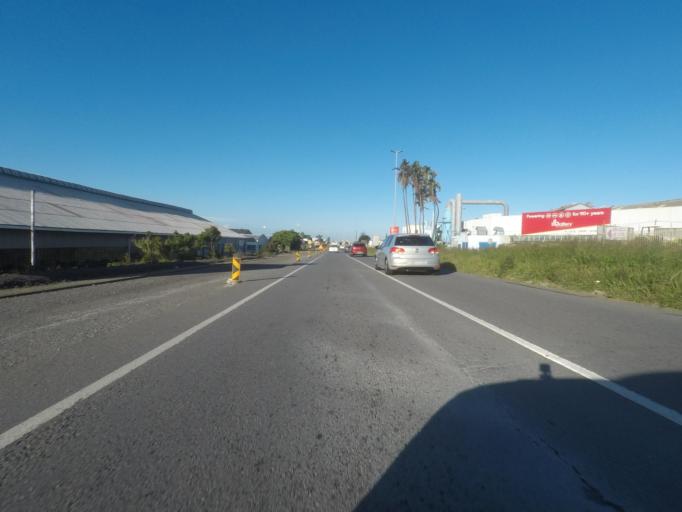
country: ZA
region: Eastern Cape
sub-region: Buffalo City Metropolitan Municipality
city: East London
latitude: -33.0333
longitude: 27.8828
